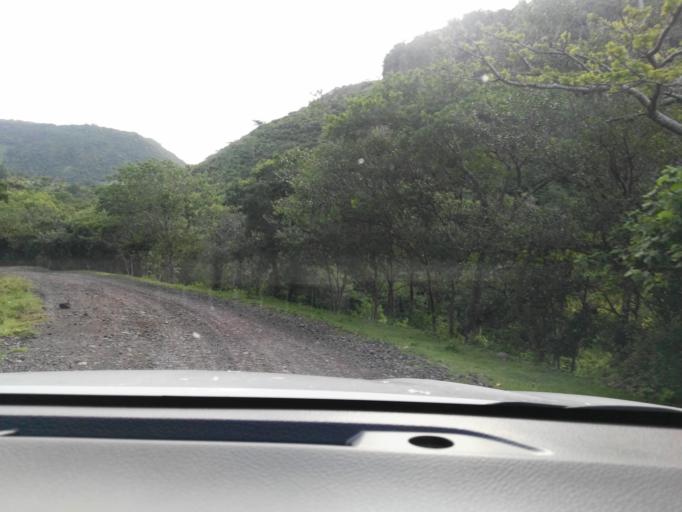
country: NI
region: Matagalpa
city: Ciudad Dario
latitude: 12.8479
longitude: -86.0469
